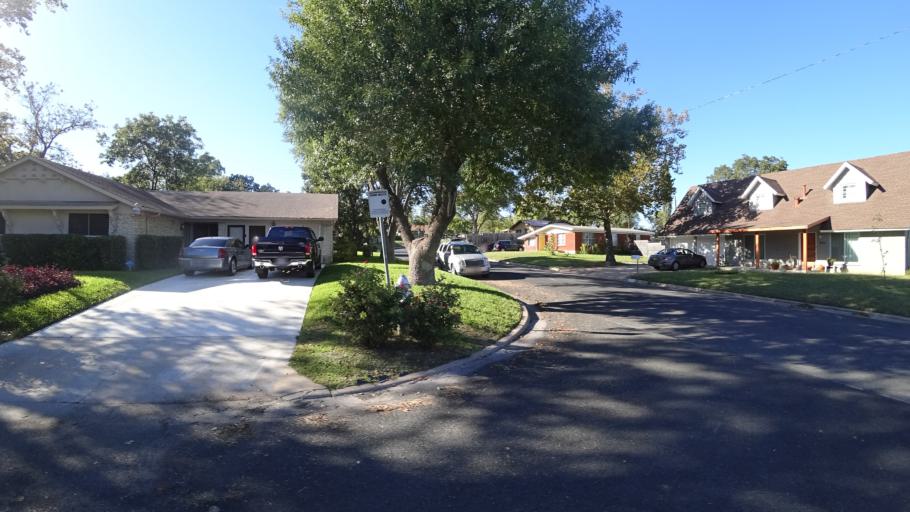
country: US
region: Texas
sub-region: Travis County
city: Austin
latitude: 30.2889
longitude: -97.6702
